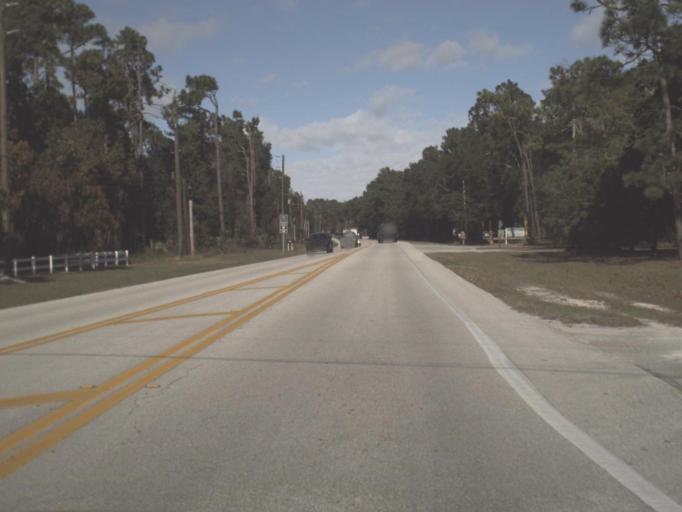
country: US
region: Florida
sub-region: Volusia County
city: Samsula-Spruce Creek
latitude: 29.0911
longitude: -81.0496
